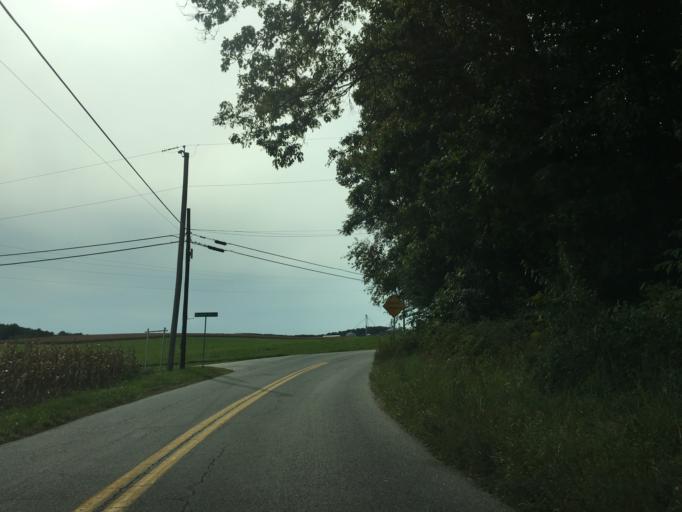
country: US
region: Maryland
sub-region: Baltimore County
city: Hunt Valley
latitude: 39.5624
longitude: -76.6699
